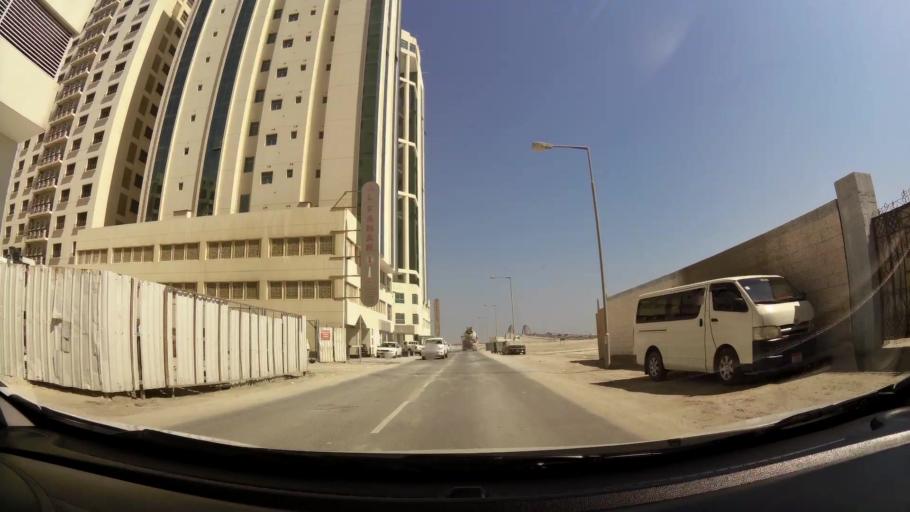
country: BH
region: Manama
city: Manama
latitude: 26.2135
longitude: 50.6192
